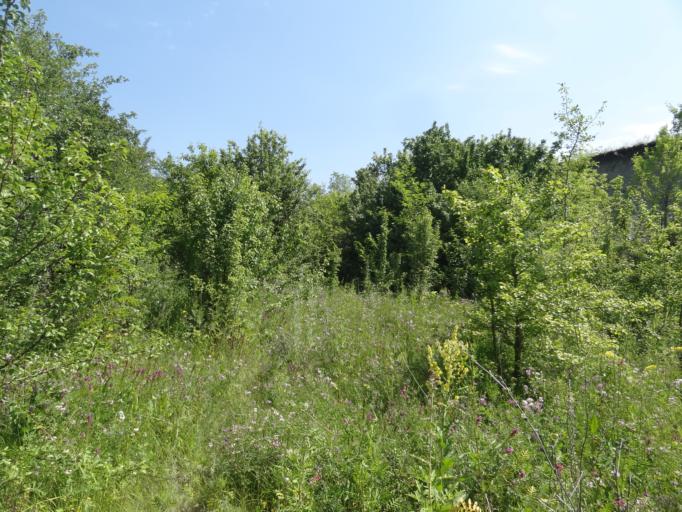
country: RU
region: Saratov
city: Sokolovyy
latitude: 51.4260
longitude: 45.7993
